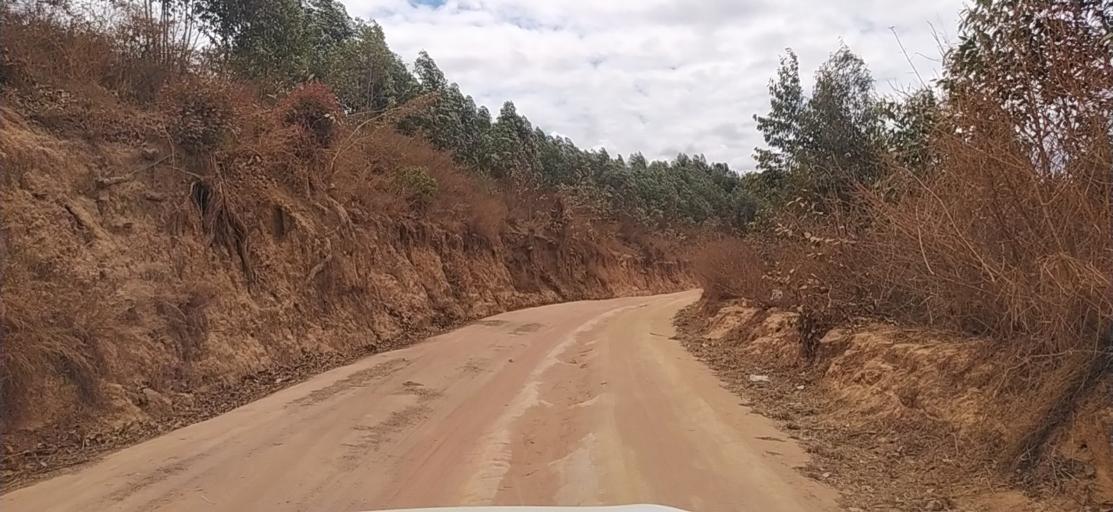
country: MG
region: Alaotra Mangoro
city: Ambatondrazaka
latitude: -18.0079
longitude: 48.2593
